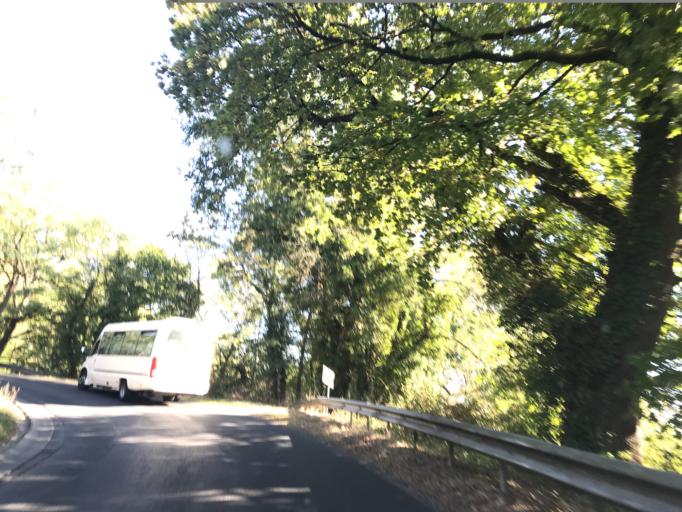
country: FR
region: Auvergne
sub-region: Departement du Puy-de-Dome
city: Courpiere
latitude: 45.7523
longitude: 3.5541
